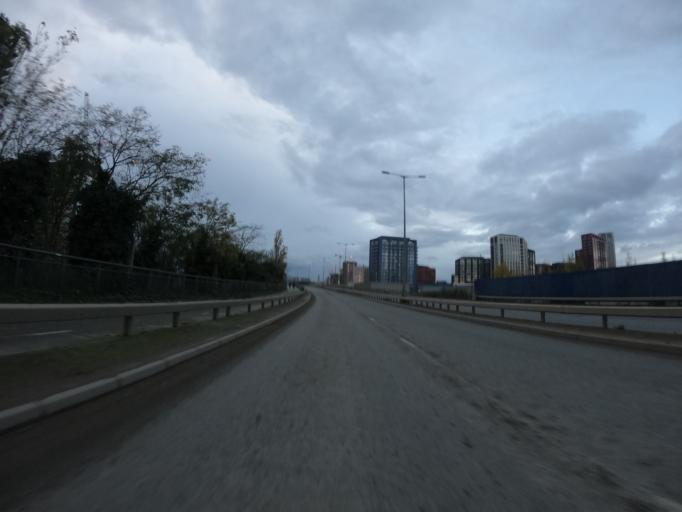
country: GB
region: England
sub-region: Greater London
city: Poplar
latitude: 51.5097
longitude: 0.0097
